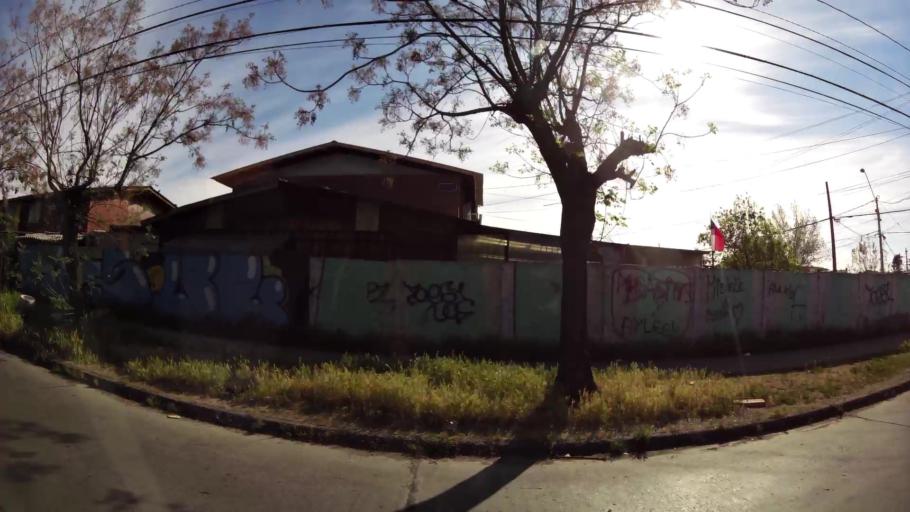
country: CL
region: Santiago Metropolitan
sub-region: Provincia de Cordillera
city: Puente Alto
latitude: -33.6213
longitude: -70.5905
